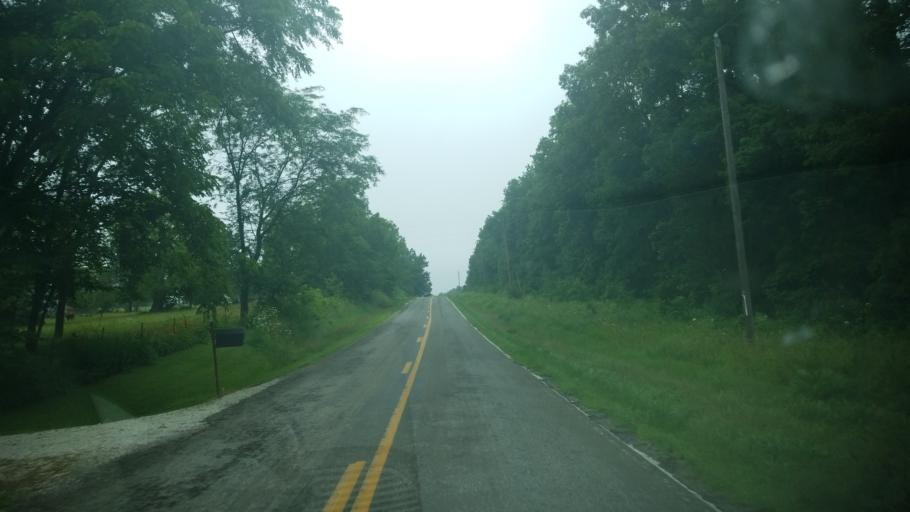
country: US
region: Missouri
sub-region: Audrain County
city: Vandalia
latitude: 39.2919
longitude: -91.3507
